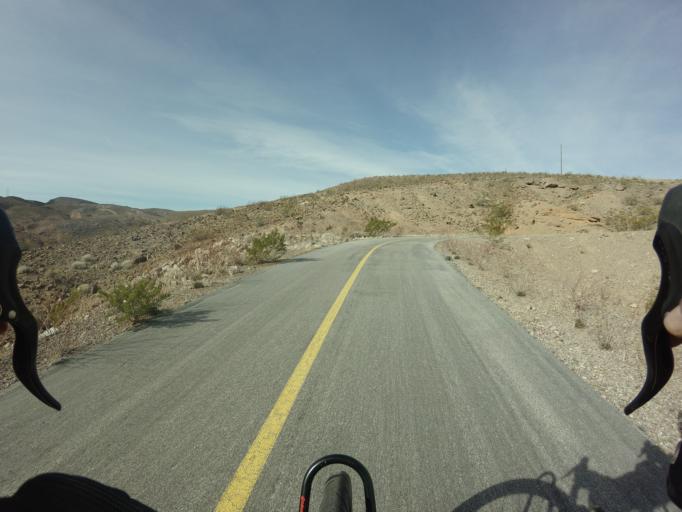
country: US
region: Nevada
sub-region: Clark County
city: Henderson
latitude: 36.1134
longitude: -114.8678
